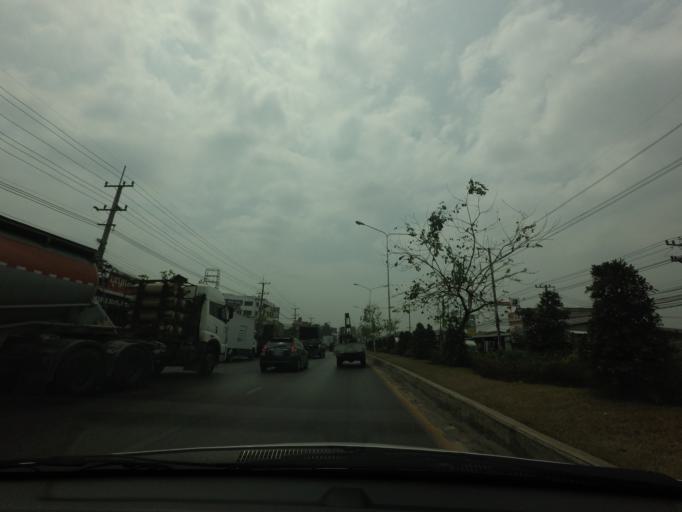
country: TH
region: Bangkok
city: Nong Khaem
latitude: 13.7334
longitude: 100.3296
